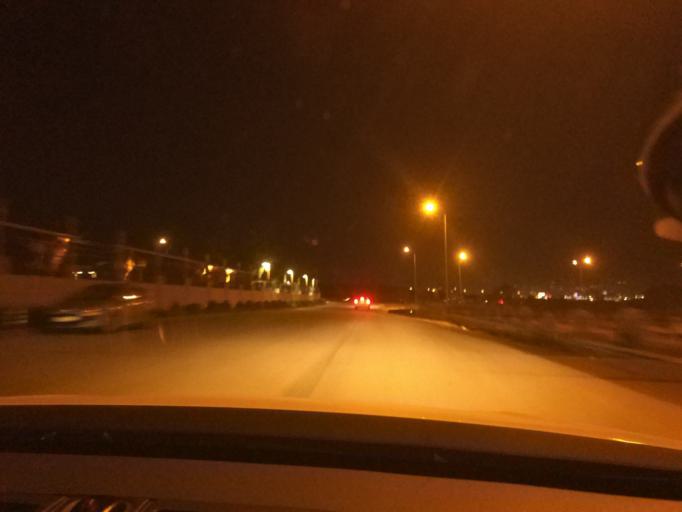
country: TR
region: Ankara
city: Batikent
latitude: 39.9132
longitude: 32.7527
